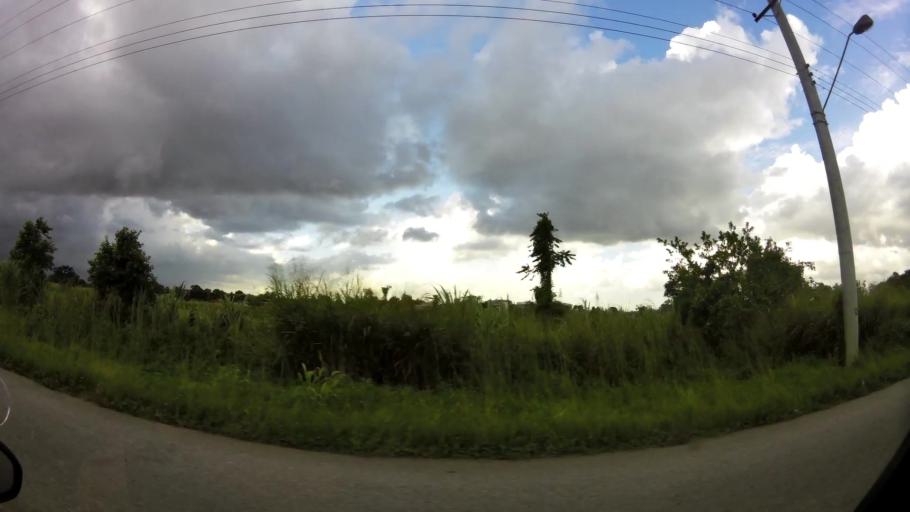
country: TT
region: City of San Fernando
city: Mon Repos
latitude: 10.2625
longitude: -61.4334
